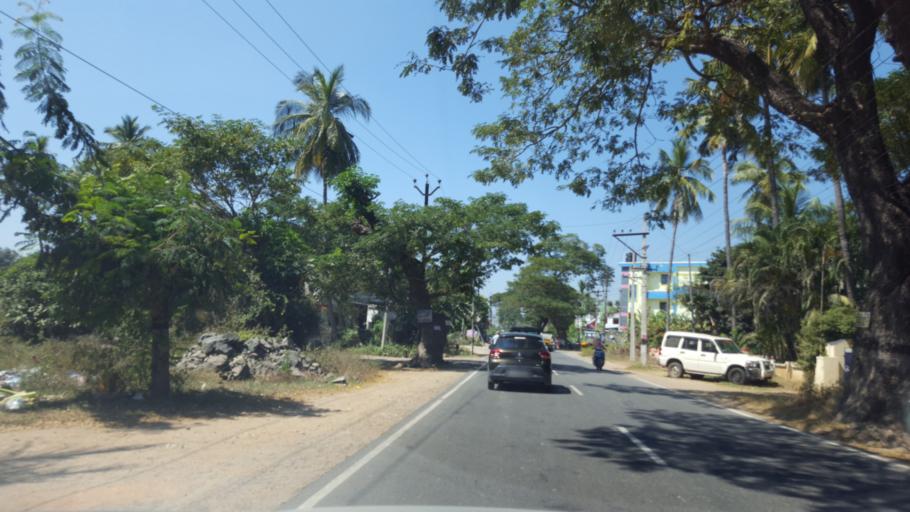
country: IN
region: Tamil Nadu
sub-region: Kancheepuram
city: Chengalpattu
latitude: 12.7122
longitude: 79.9601
